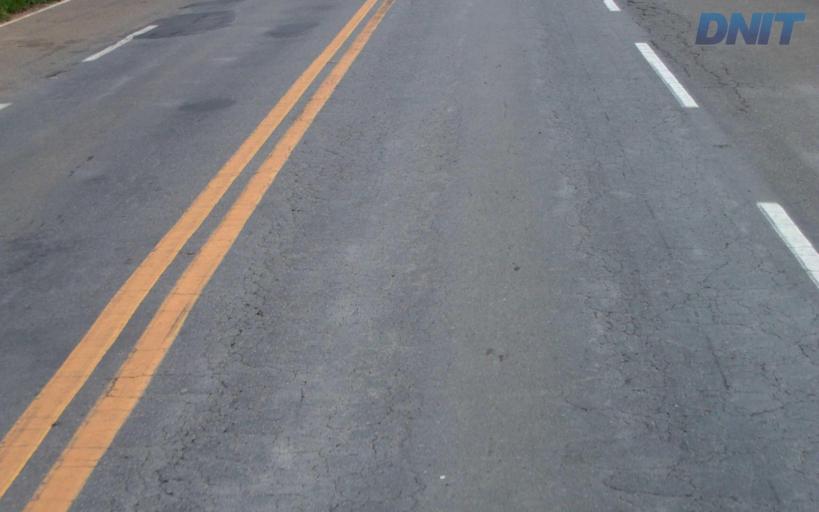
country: BR
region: Minas Gerais
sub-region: Governador Valadares
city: Governador Valadares
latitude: -19.0145
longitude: -42.1407
